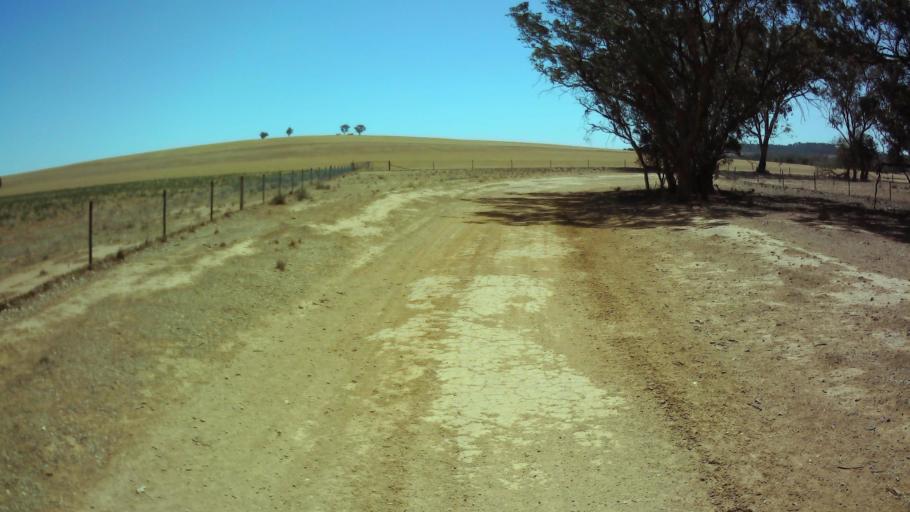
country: AU
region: New South Wales
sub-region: Weddin
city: Grenfell
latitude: -33.9815
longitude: 148.1656
